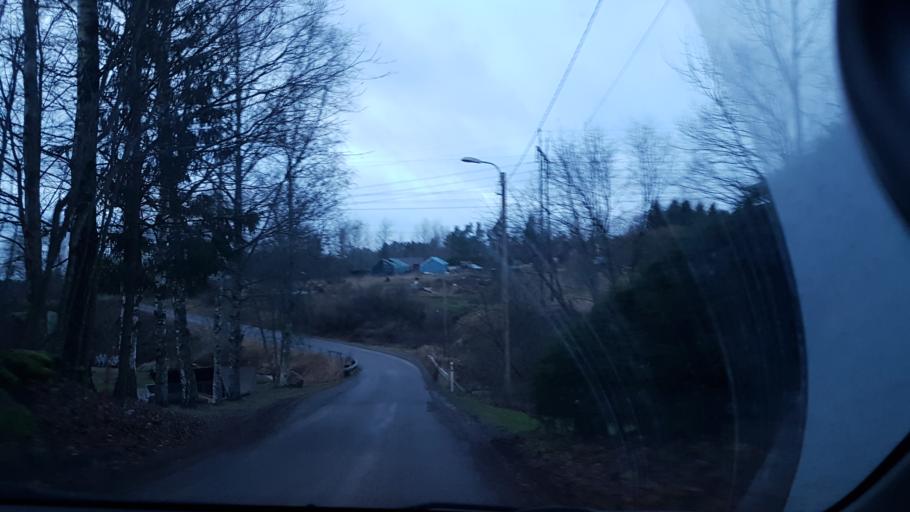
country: FI
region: Uusimaa
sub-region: Helsinki
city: Vantaa
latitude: 60.2836
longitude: 25.1410
